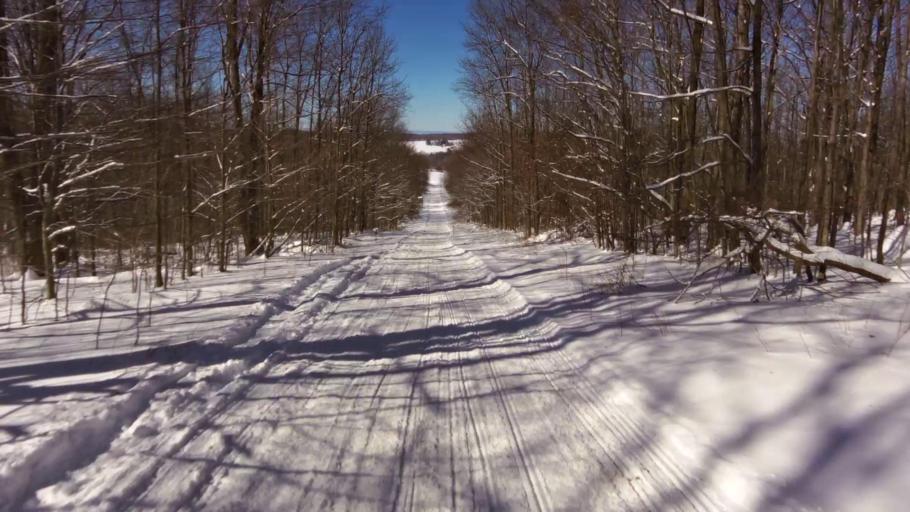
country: US
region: New York
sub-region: Chautauqua County
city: Mayville
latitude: 42.2462
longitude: -79.4201
